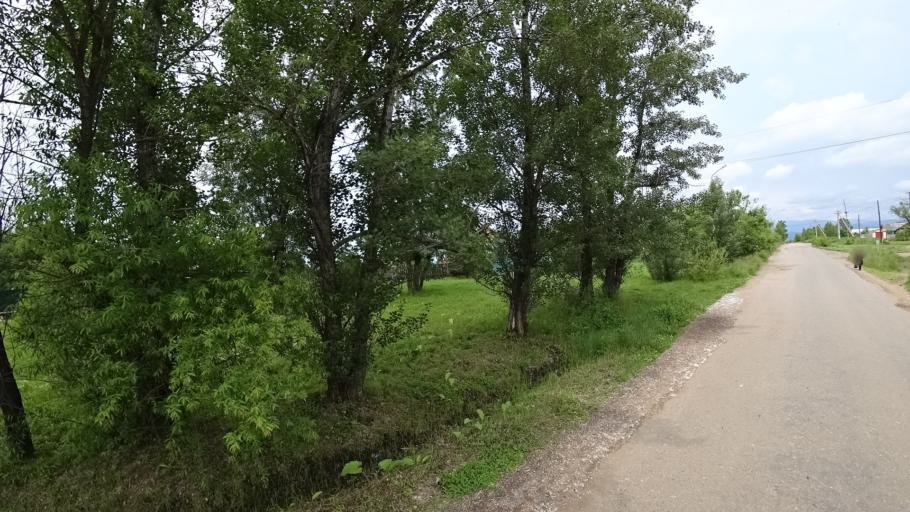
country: RU
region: Primorskiy
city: Novosysoyevka
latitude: 44.2313
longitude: 133.3604
